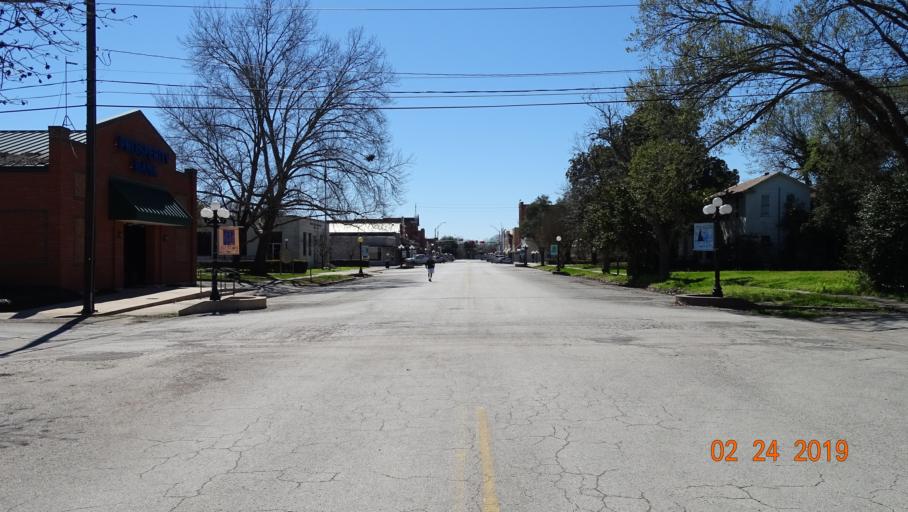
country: US
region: Texas
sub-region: Bastrop County
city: Smithville
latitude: 30.0102
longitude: -97.1586
